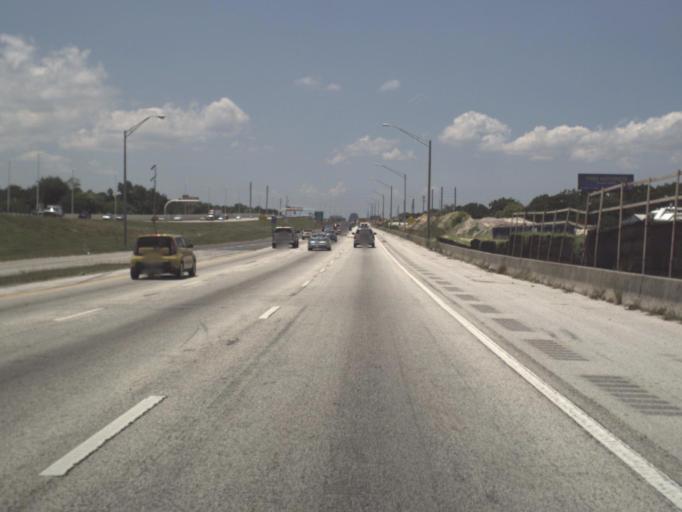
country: US
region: Florida
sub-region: Hillsborough County
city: Tampa
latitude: 27.9561
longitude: -82.4863
